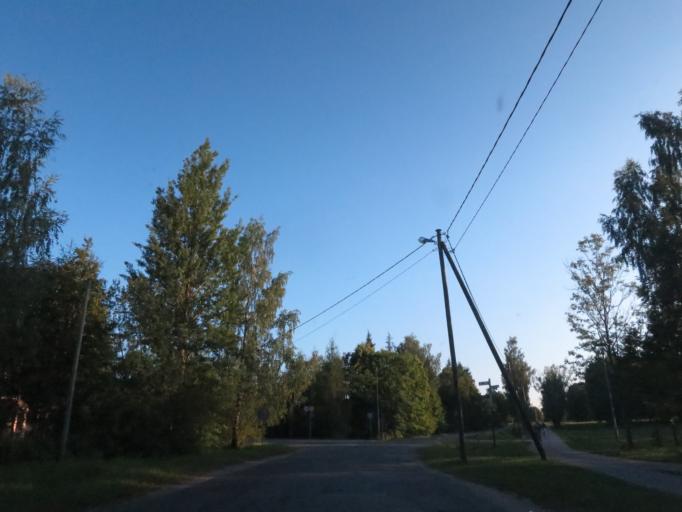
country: LV
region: Sigulda
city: Sigulda
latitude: 57.1653
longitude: 24.8611
